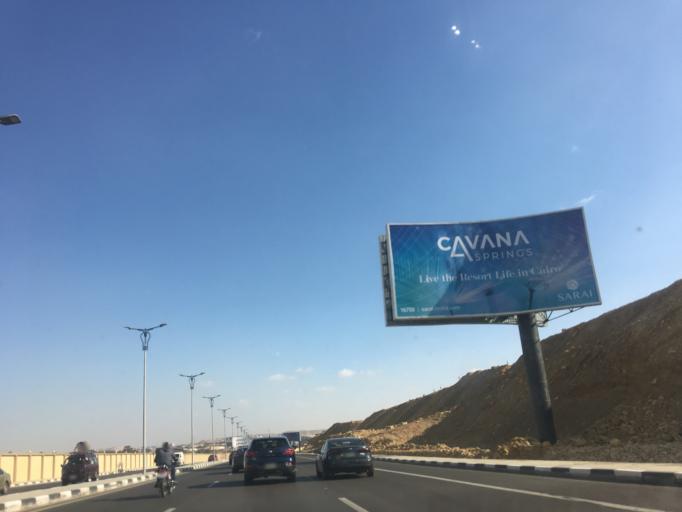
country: EG
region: Muhafazat al Qahirah
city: Cairo
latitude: 30.0276
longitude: 31.3146
